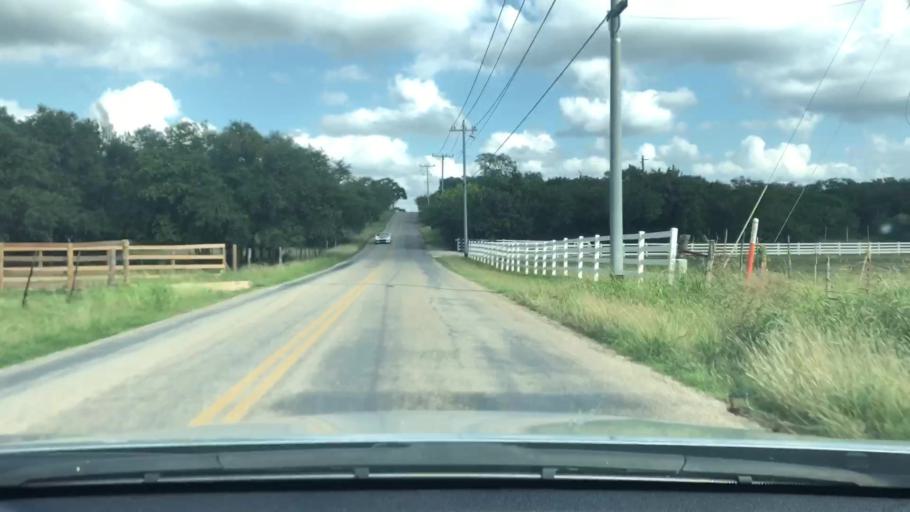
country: US
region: Texas
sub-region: Bexar County
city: Fair Oaks Ranch
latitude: 29.7851
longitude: -98.6329
